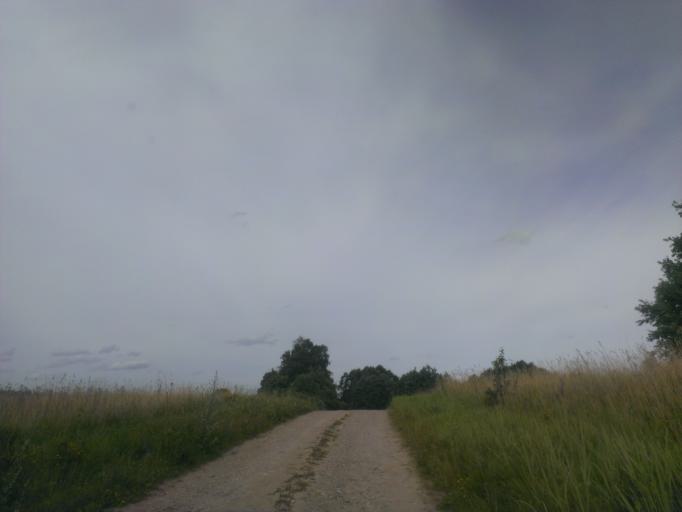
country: LV
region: Ligatne
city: Ligatne
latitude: 57.2263
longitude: 25.0097
